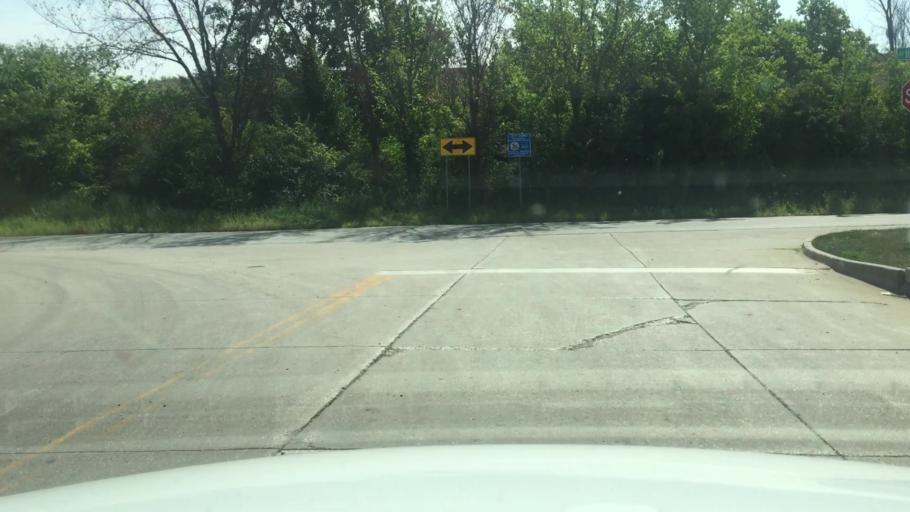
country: US
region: Missouri
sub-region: Jackson County
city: Greenwood
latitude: 38.8791
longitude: -94.3576
